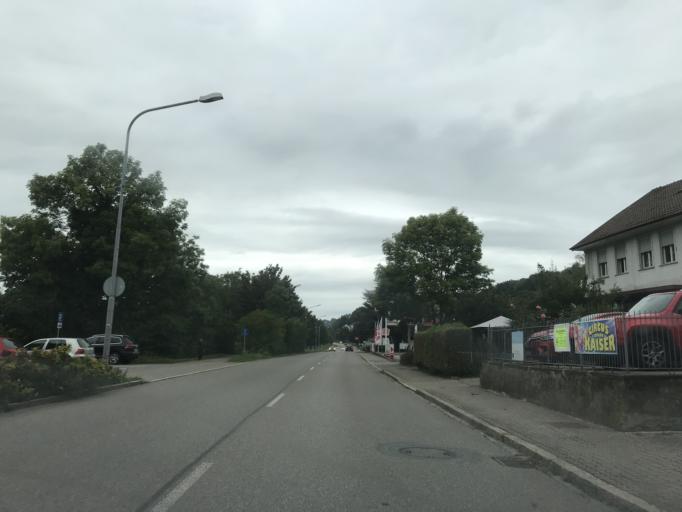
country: DE
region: Baden-Wuerttemberg
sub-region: Freiburg Region
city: Murg
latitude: 47.5541
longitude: 8.0173
